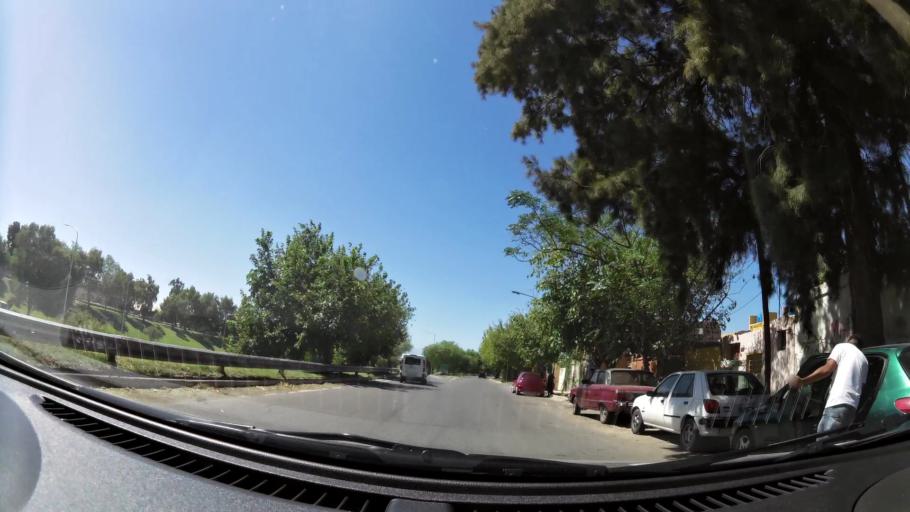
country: AR
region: San Juan
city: San Juan
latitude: -31.5165
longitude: -68.5240
